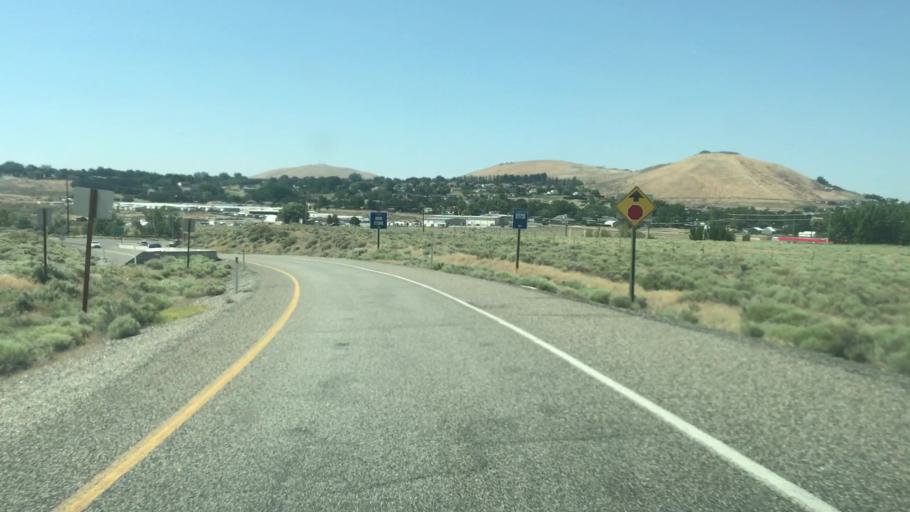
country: US
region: Washington
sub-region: Benton County
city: Richland
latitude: 46.1940
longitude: -119.2643
